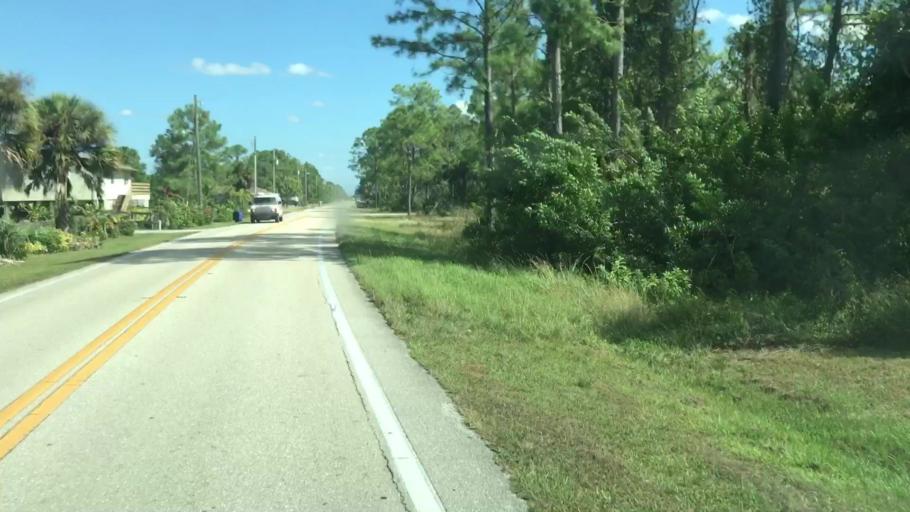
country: US
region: Florida
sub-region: Lee County
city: Lehigh Acres
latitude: 26.6427
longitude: -81.6576
